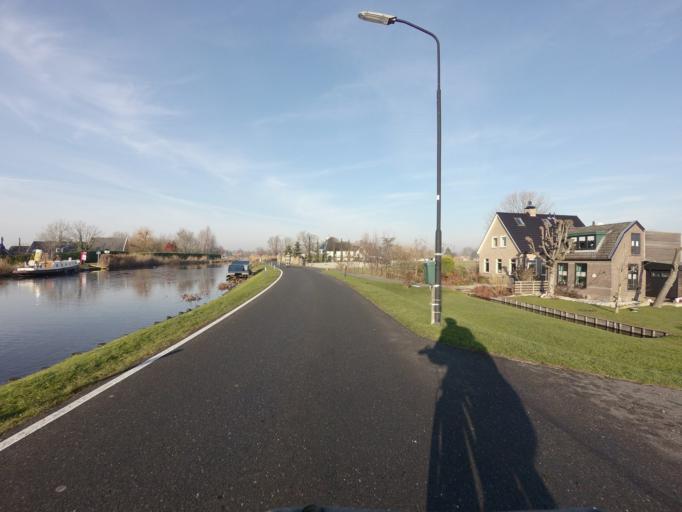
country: NL
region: Utrecht
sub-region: Gemeente De Ronde Venen
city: Mijdrecht
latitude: 52.1942
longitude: 4.8239
